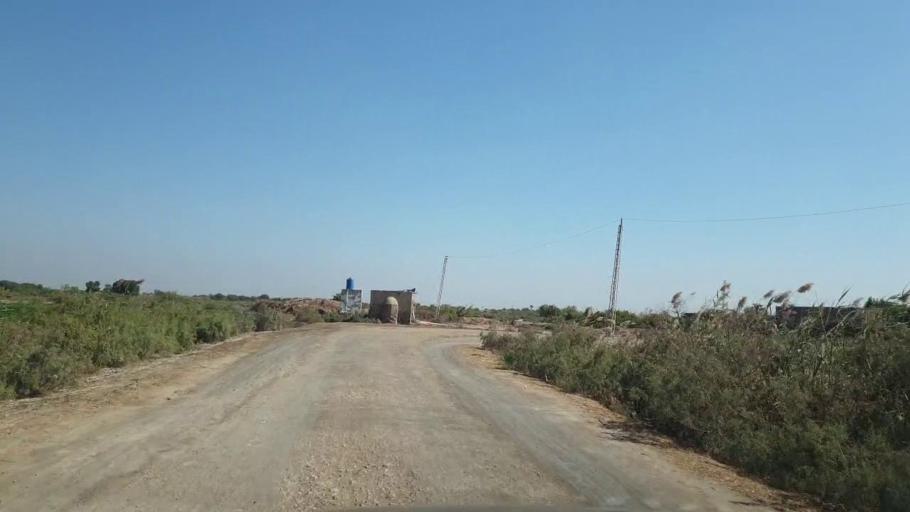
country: PK
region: Sindh
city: Mirpur Khas
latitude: 25.5969
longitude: 69.1041
